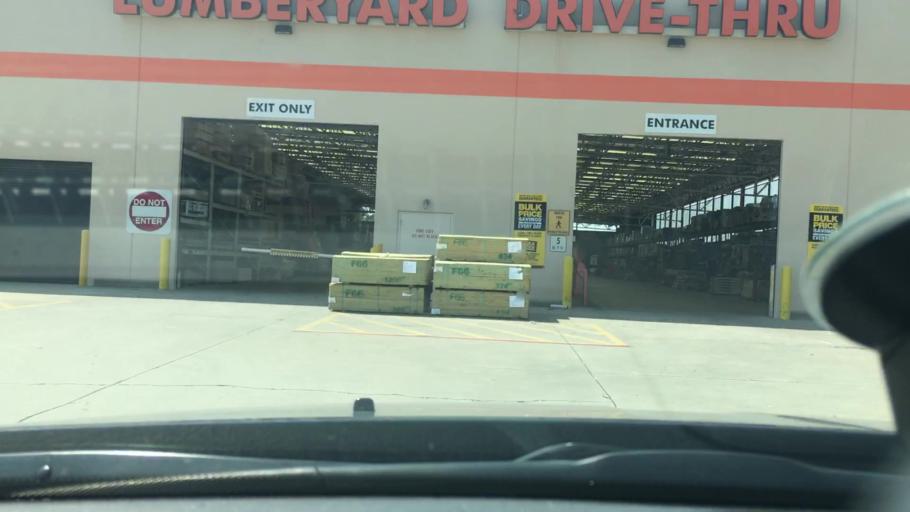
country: US
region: Oklahoma
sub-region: Pontotoc County
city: Ada
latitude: 34.7884
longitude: -96.6721
